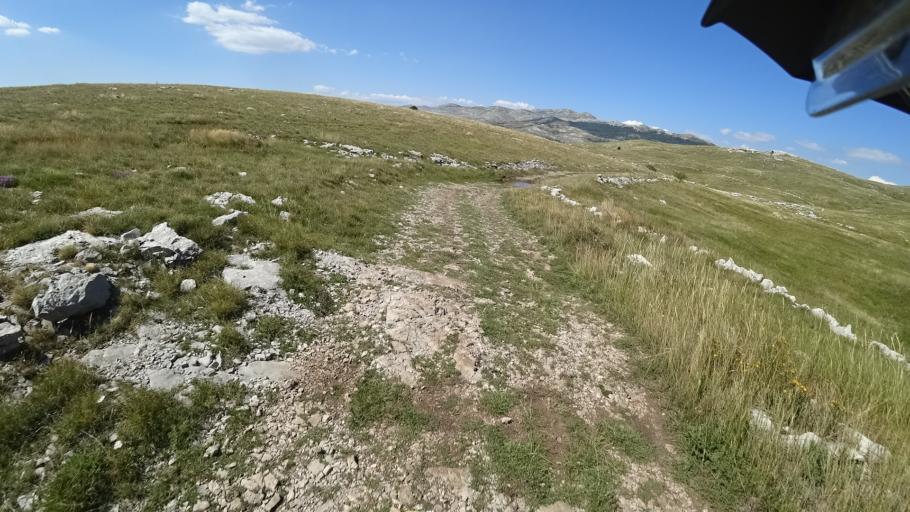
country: HR
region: Splitsko-Dalmatinska
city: Hrvace
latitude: 43.8872
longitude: 16.6378
